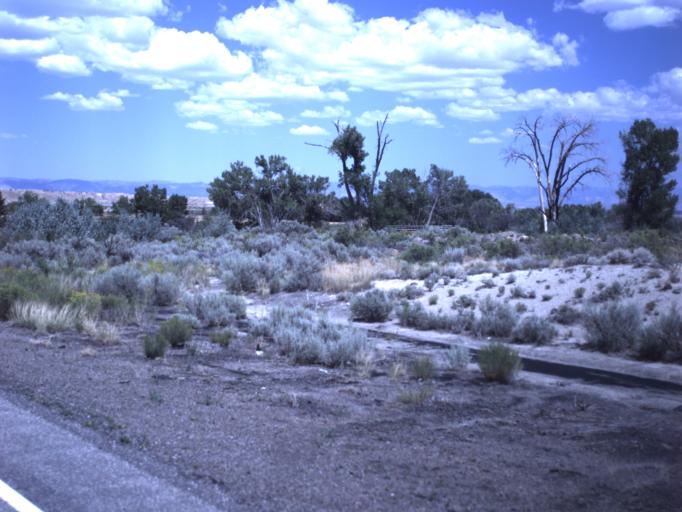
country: US
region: Utah
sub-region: Carbon County
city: Price
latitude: 39.5211
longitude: -110.8257
